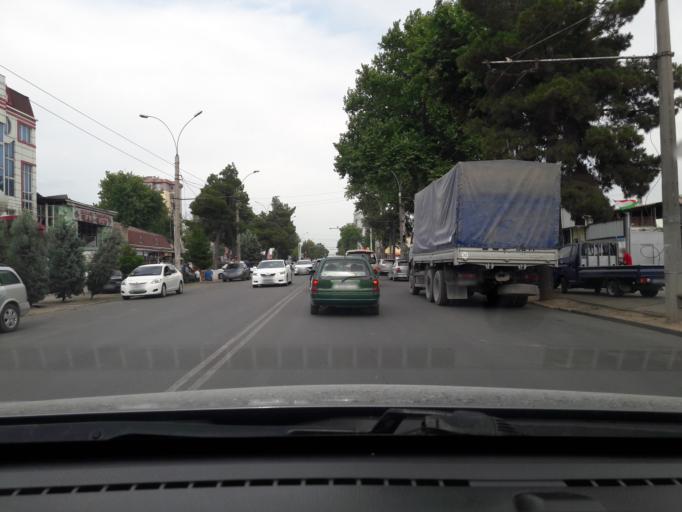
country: TJ
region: Dushanbe
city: Dushanbe
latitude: 38.5461
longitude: 68.7536
